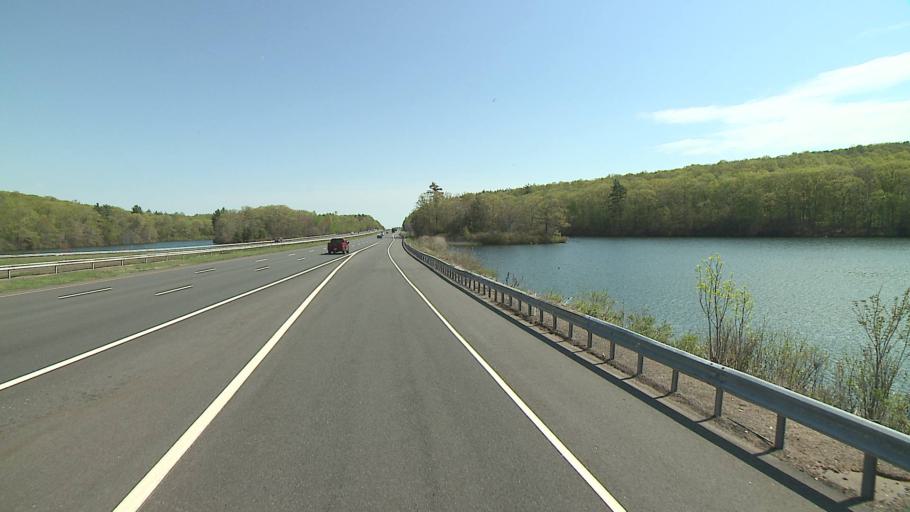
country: US
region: Connecticut
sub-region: Tolland County
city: Stafford
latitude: 41.9609
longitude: -72.1938
